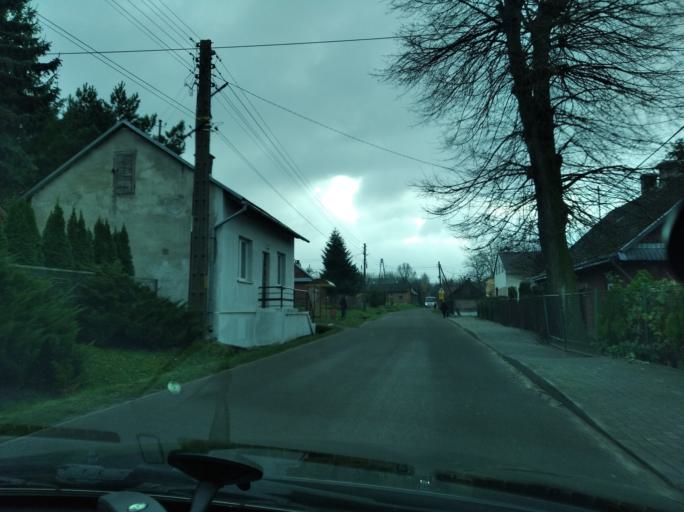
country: PL
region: Subcarpathian Voivodeship
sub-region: Powiat przeworski
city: Sietesz
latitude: 49.9899
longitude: 22.3508
